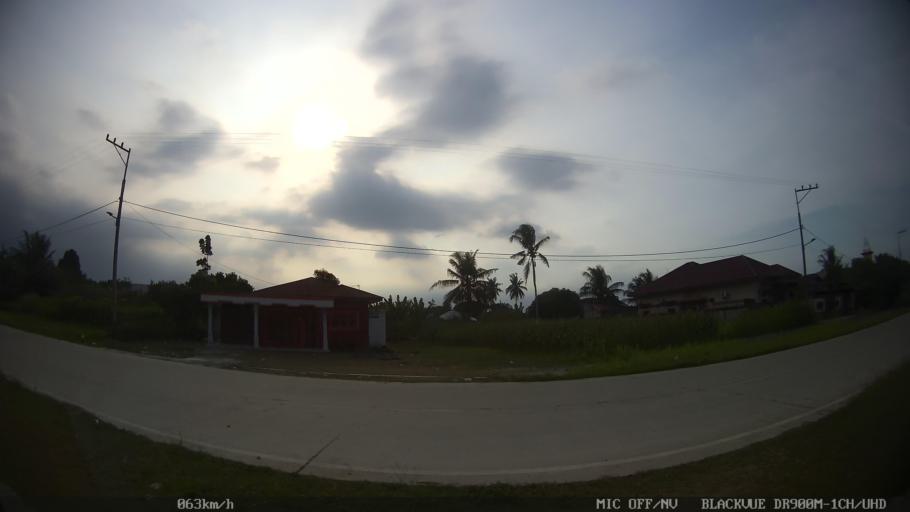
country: ID
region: North Sumatra
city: Binjai
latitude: 3.6031
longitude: 98.5338
